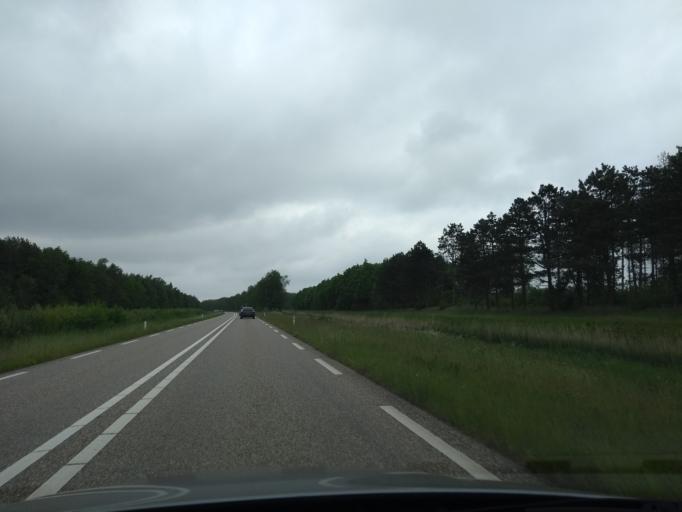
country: NL
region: Groningen
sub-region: Gemeente De Marne
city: Ulrum
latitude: 53.3987
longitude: 6.2331
